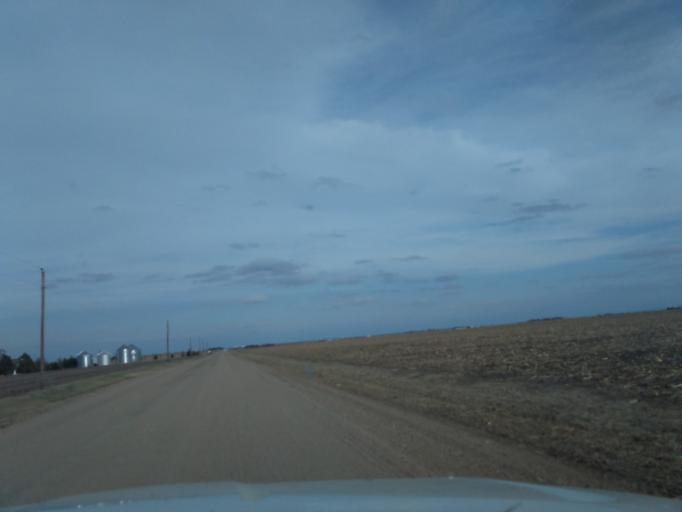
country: US
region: Nebraska
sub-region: Saline County
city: Wilber
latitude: 40.3208
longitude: -96.9157
